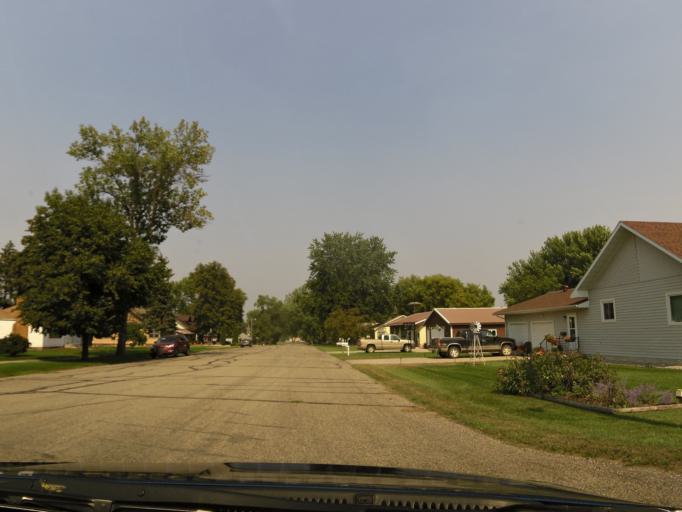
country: US
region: South Dakota
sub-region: Roberts County
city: Sisseton
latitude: 46.0755
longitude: -97.1446
